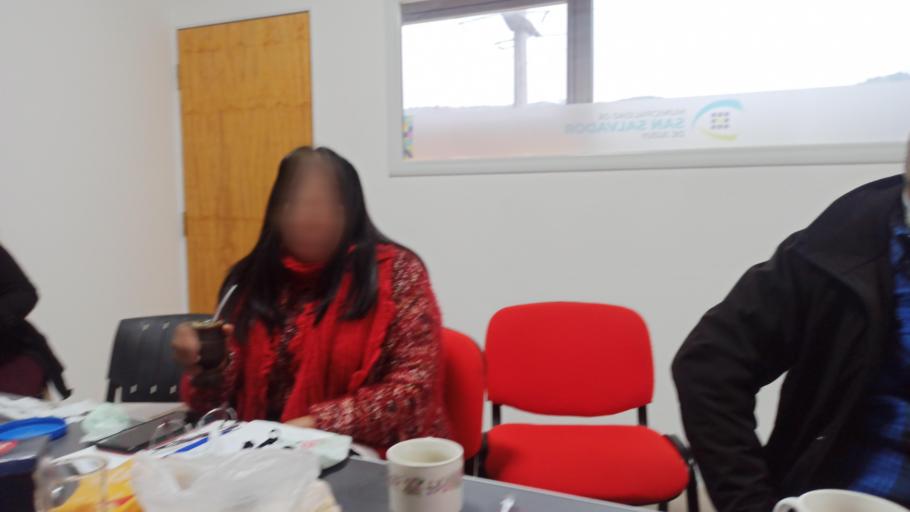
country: AR
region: Jujuy
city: San Salvador de Jujuy
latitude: -24.1991
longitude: -65.3119
